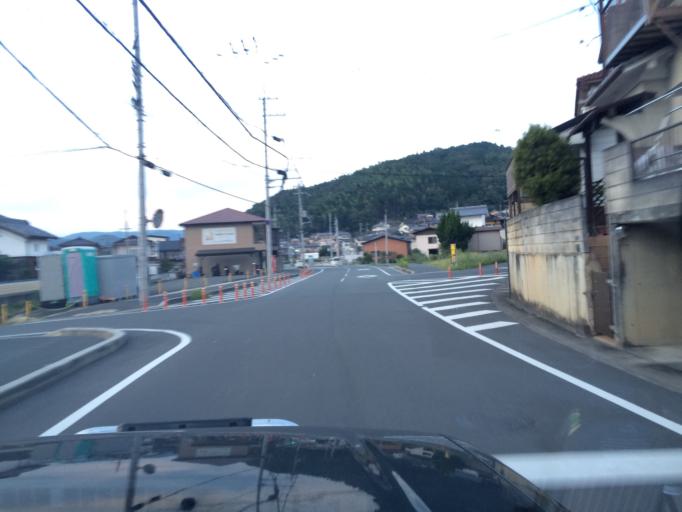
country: JP
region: Kyoto
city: Kameoka
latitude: 35.0984
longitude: 135.4747
